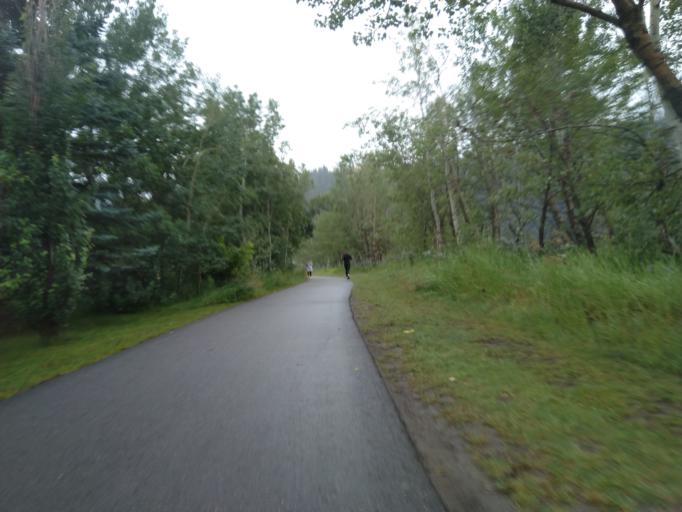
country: CA
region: Alberta
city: Cochrane
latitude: 51.1748
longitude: -114.4775
